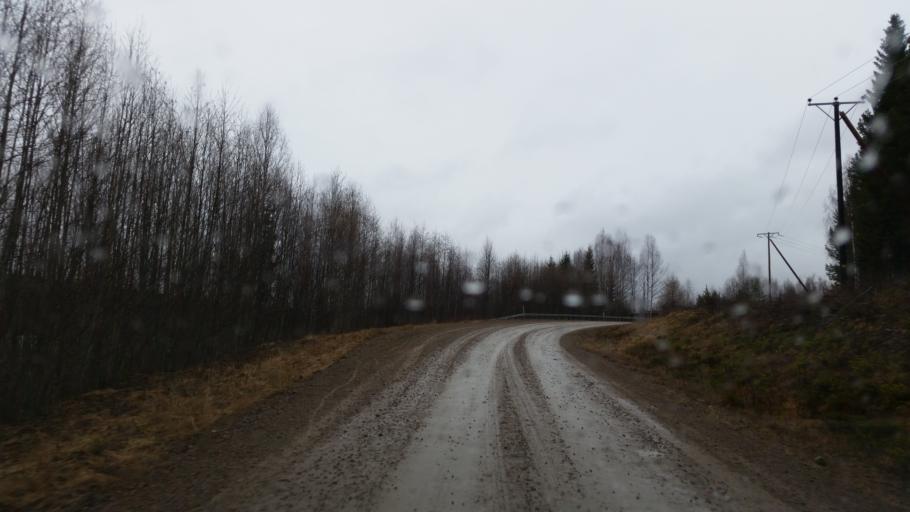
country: SE
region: Vaesternorrland
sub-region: Ange Kommun
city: Ange
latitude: 62.1556
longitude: 15.6632
